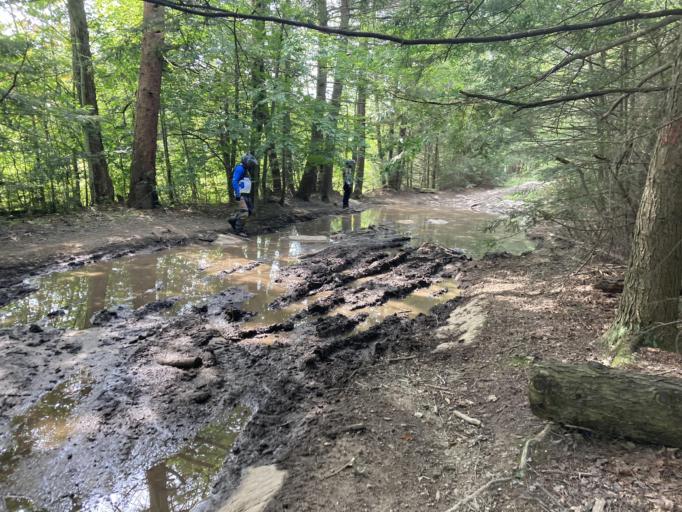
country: US
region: Vermont
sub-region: Franklin County
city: Enosburg Falls
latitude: 44.9622
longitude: -72.9280
